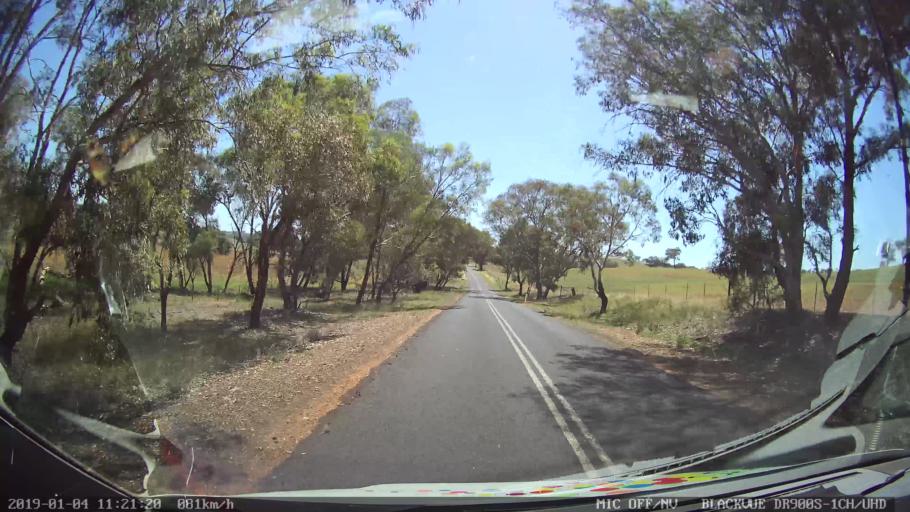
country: AU
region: New South Wales
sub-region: Cabonne
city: Molong
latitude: -33.1553
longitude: 148.7098
